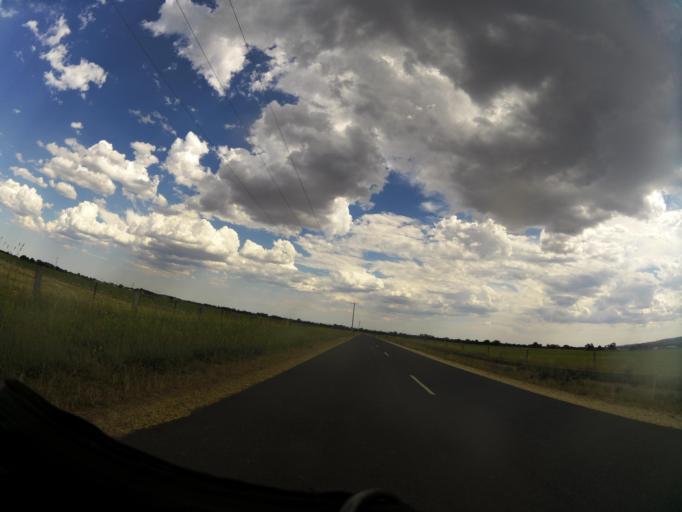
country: AU
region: Victoria
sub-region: Wellington
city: Heyfield
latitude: -37.9920
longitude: 146.6927
